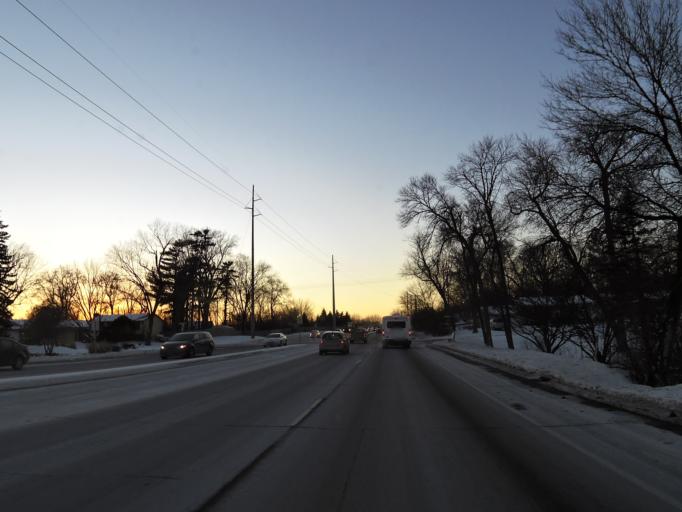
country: US
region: Minnesota
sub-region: Dakota County
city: Apple Valley
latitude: 44.7321
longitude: -93.2467
